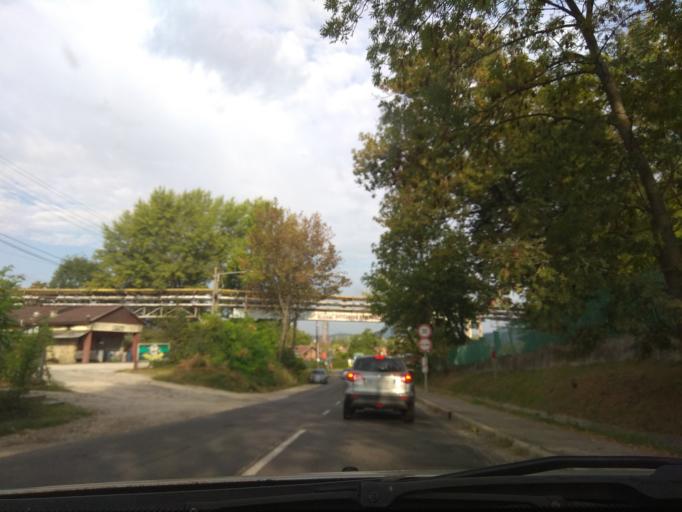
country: HU
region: Borsod-Abauj-Zemplen
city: Miskolc
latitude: 48.0885
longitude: 20.7285
